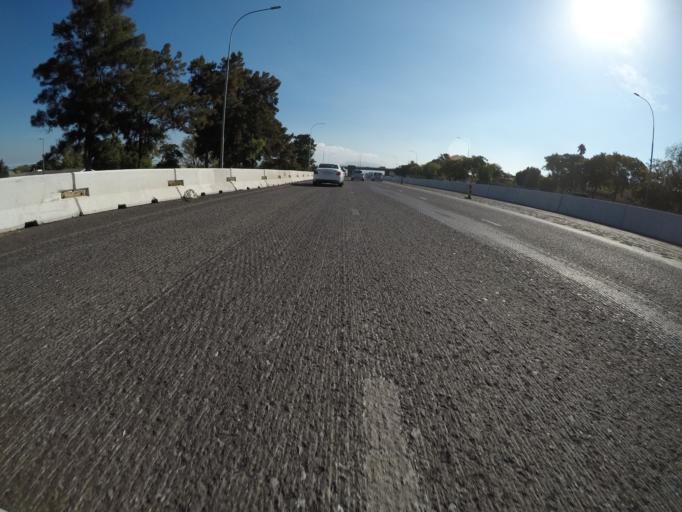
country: ZA
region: Western Cape
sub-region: City of Cape Town
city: Kraaifontein
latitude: -33.8815
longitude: 18.6485
